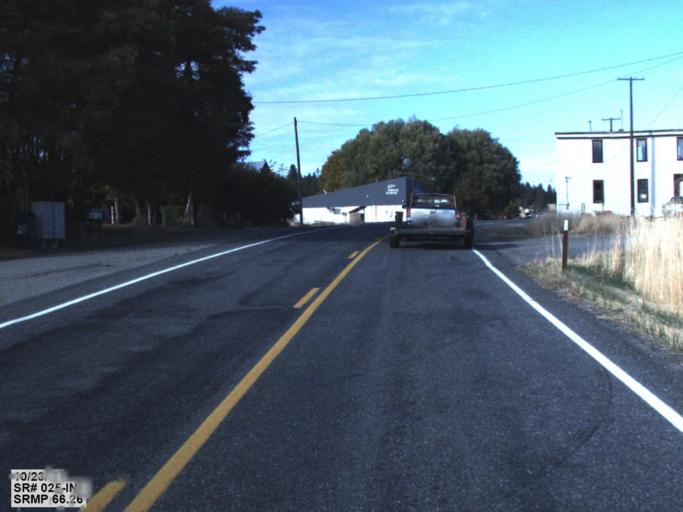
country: US
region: Washington
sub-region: Stevens County
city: Kettle Falls
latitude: 48.4277
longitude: -118.1706
